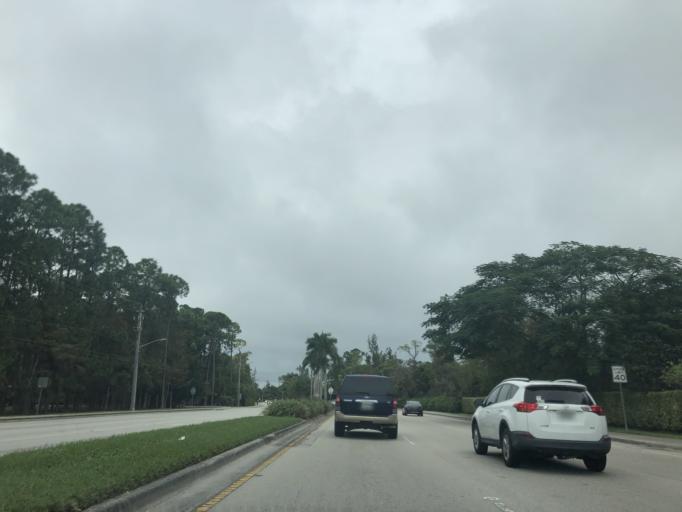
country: US
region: Florida
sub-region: Palm Beach County
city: Wellington
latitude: 26.6738
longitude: -80.2478
